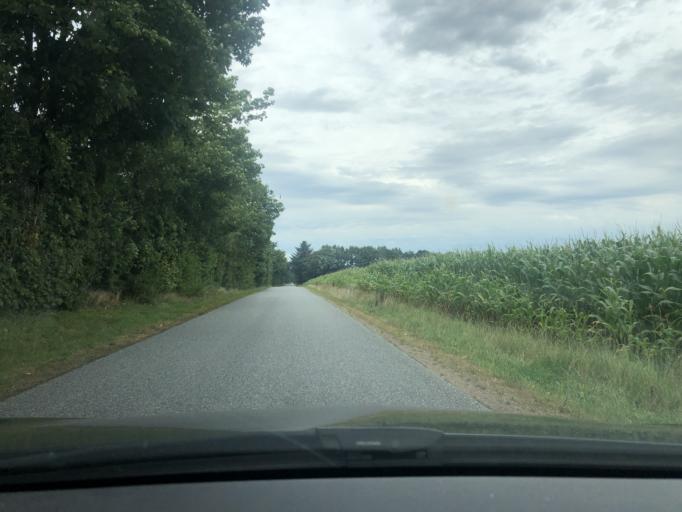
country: DK
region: South Denmark
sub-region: Varde Kommune
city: Olgod
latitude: 55.8093
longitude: 8.6808
